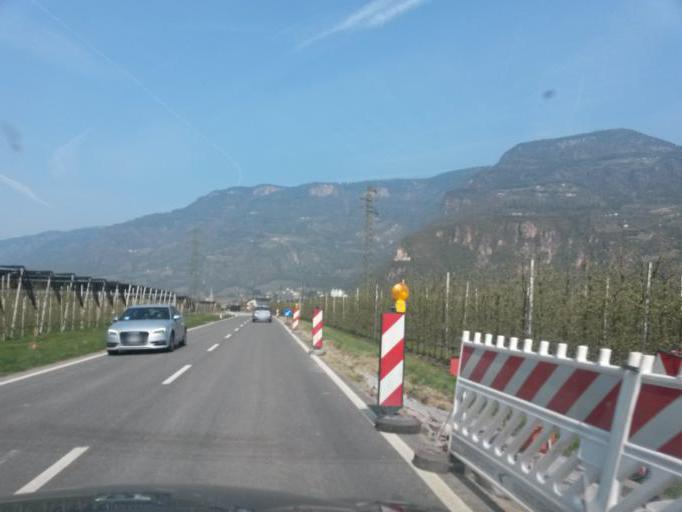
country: IT
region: Trentino-Alto Adige
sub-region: Bolzano
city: Andriano
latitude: 46.5136
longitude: 11.2467
